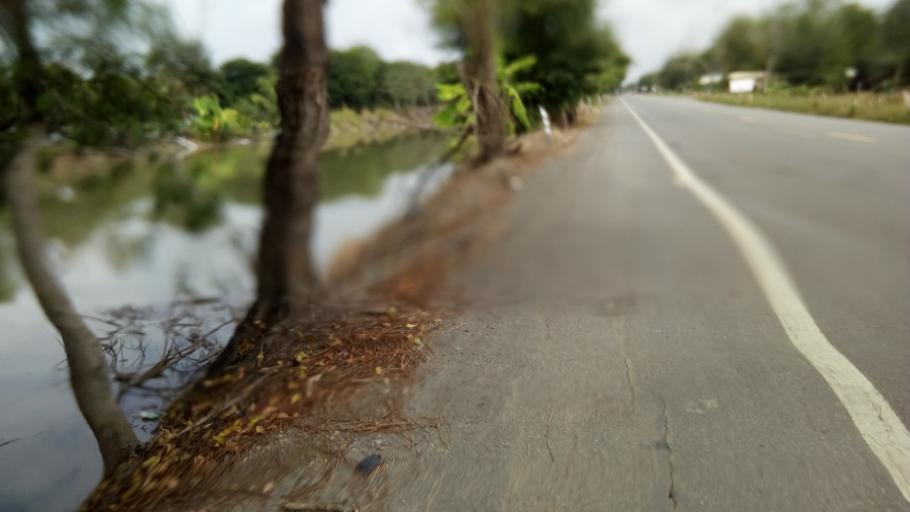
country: TH
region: Pathum Thani
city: Nong Suea
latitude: 14.1809
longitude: 100.8236
